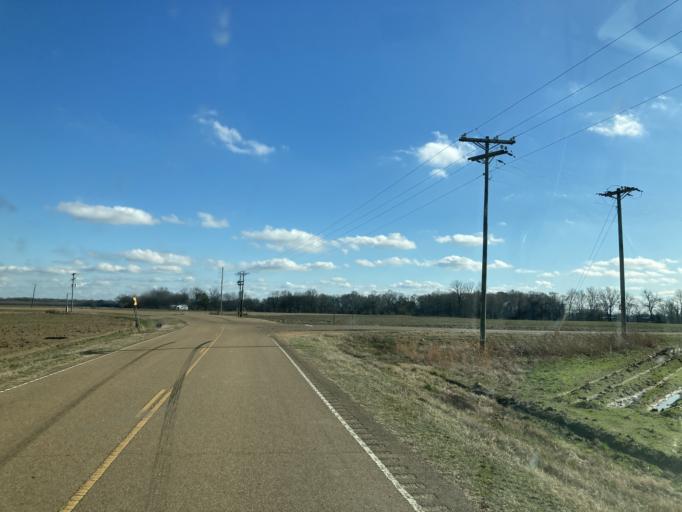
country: US
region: Mississippi
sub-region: Yazoo County
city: Yazoo City
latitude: 32.9626
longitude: -90.4941
